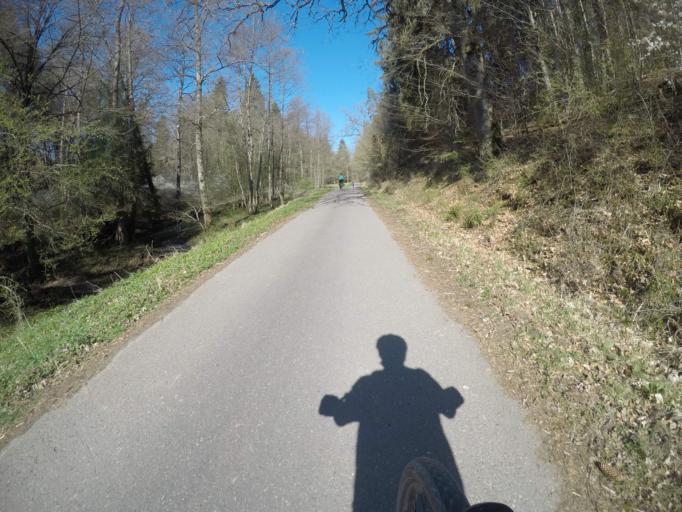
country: DE
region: Baden-Wuerttemberg
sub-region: Tuebingen Region
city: Tuebingen
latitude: 48.5583
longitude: 9.0094
